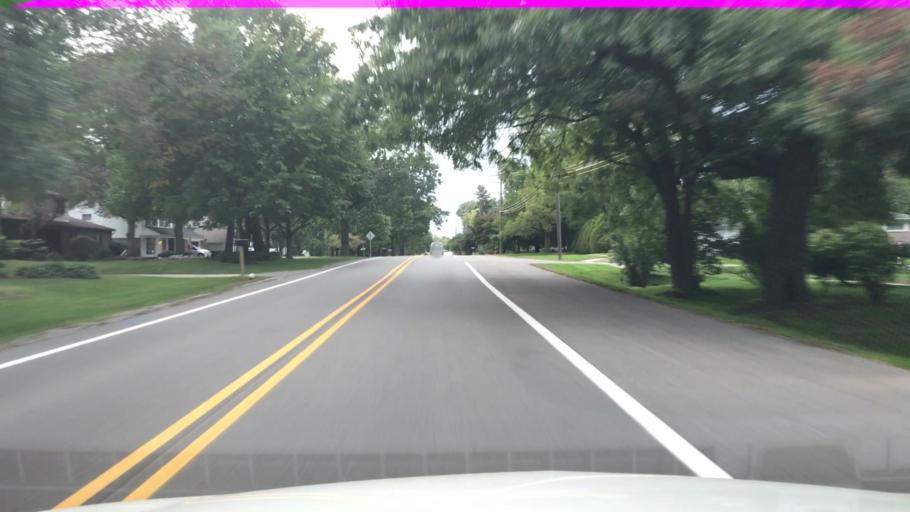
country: US
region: Michigan
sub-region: Oakland County
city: Rochester
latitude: 42.6827
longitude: -83.0867
